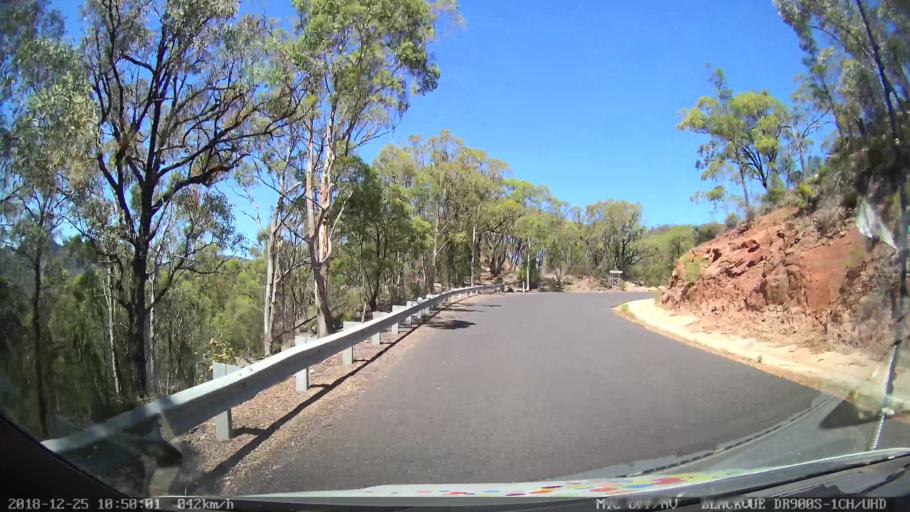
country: AU
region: New South Wales
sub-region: Upper Hunter Shire
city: Merriwa
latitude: -32.4481
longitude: 150.2691
